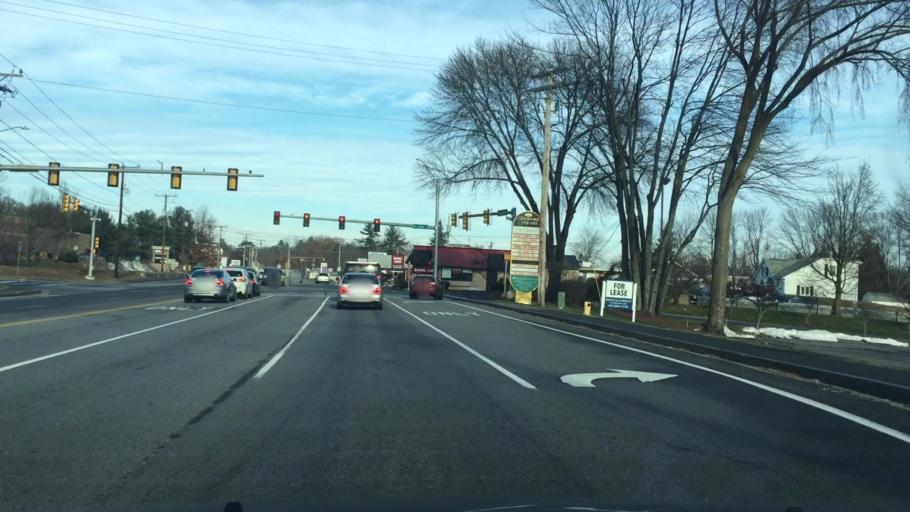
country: US
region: New Hampshire
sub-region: Hillsborough County
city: Bedford
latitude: 42.9635
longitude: -71.4802
